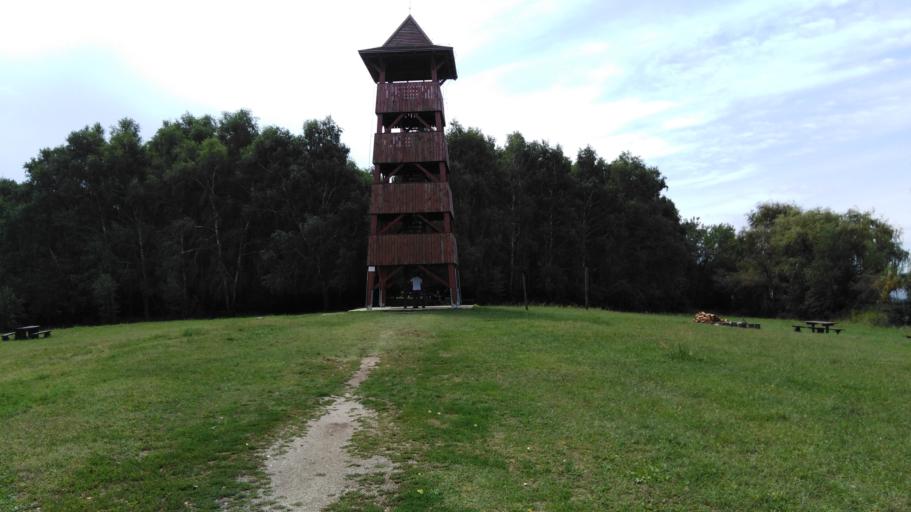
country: HU
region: Zala
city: Zalakomar
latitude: 46.6130
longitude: 17.1657
